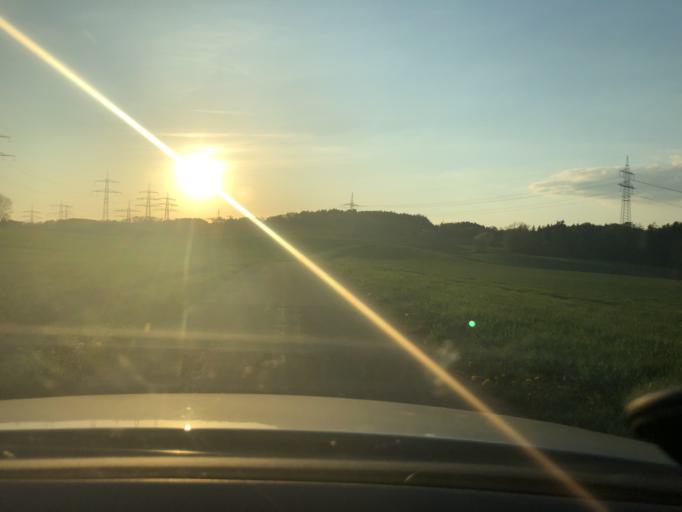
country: DE
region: Baden-Wuerttemberg
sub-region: Freiburg Region
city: Waldshut-Tiengen
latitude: 47.6500
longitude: 8.1860
